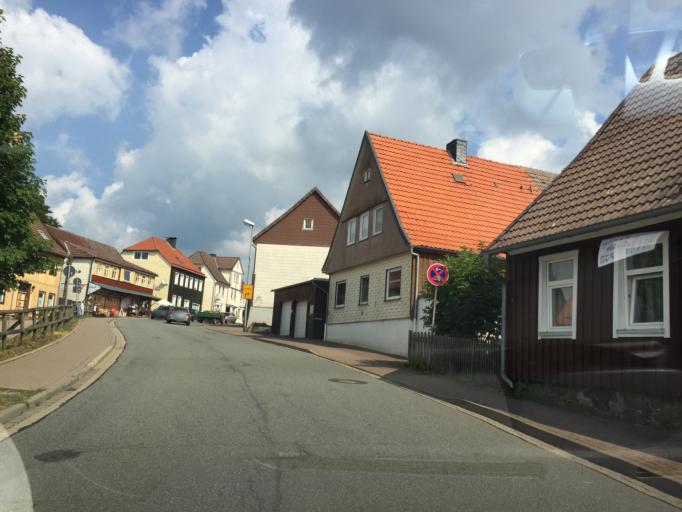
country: DE
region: Lower Saxony
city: Zorge
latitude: 51.6634
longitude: 10.6680
